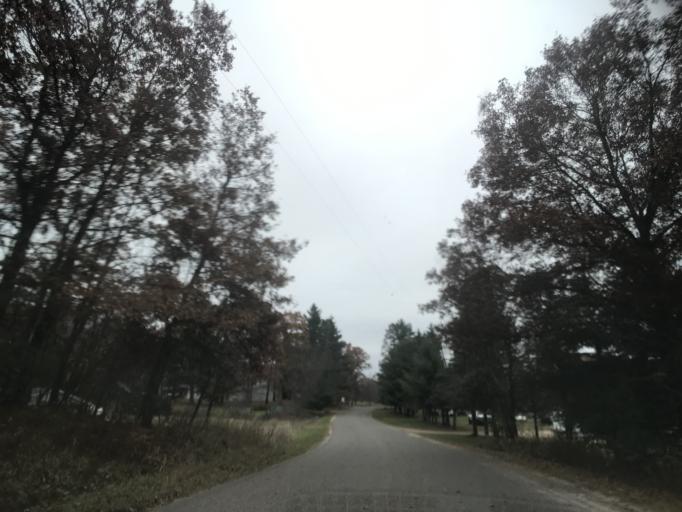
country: US
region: Michigan
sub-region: Dickinson County
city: Kingsford
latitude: 45.3857
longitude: -88.3223
